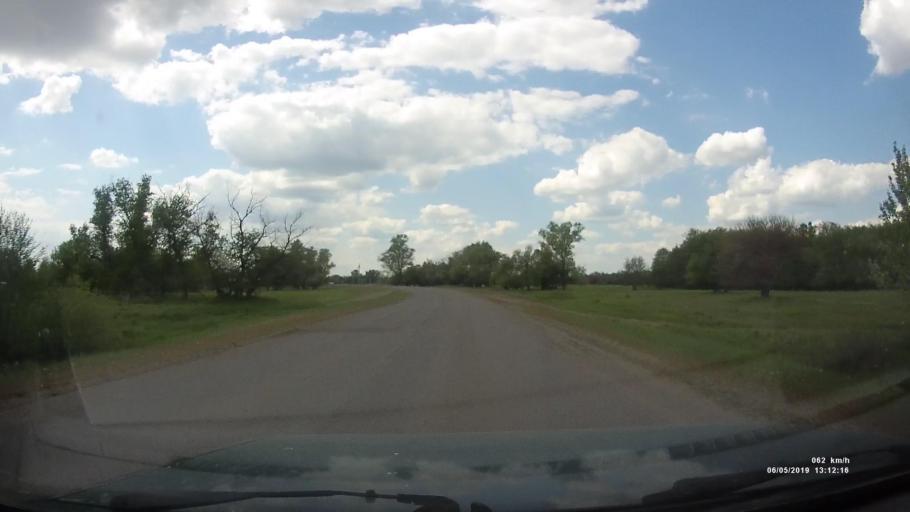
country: RU
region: Rostov
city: Ust'-Donetskiy
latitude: 47.7552
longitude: 40.9493
